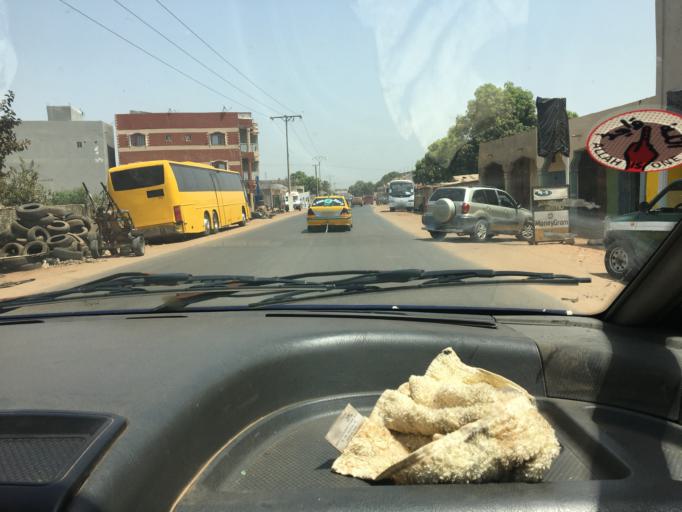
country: GM
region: Western
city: Abuko
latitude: 13.3869
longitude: -16.6769
